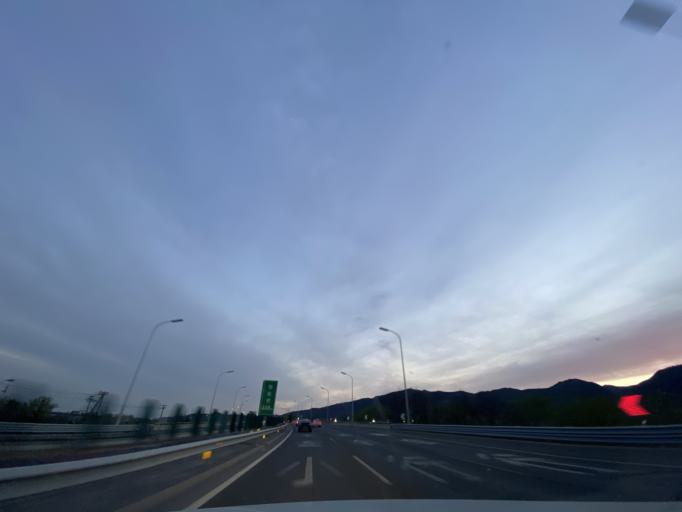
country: CN
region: Beijing
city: Xiangshan
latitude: 39.9933
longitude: 116.2179
